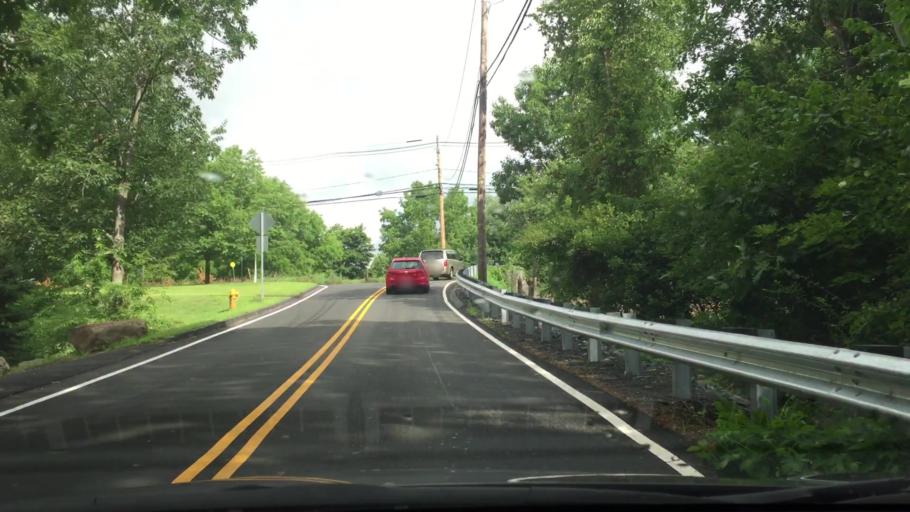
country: US
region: Massachusetts
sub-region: Middlesex County
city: Littleton Common
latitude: 42.5232
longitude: -71.4598
